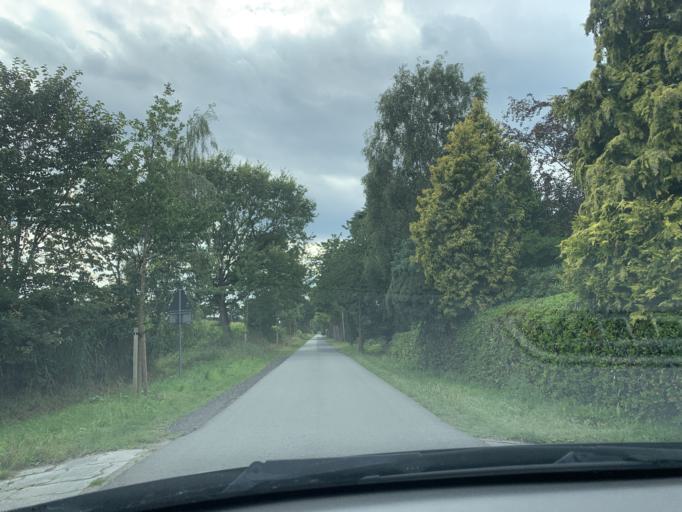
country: DE
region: Lower Saxony
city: Westerstede
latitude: 53.2537
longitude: 7.8847
